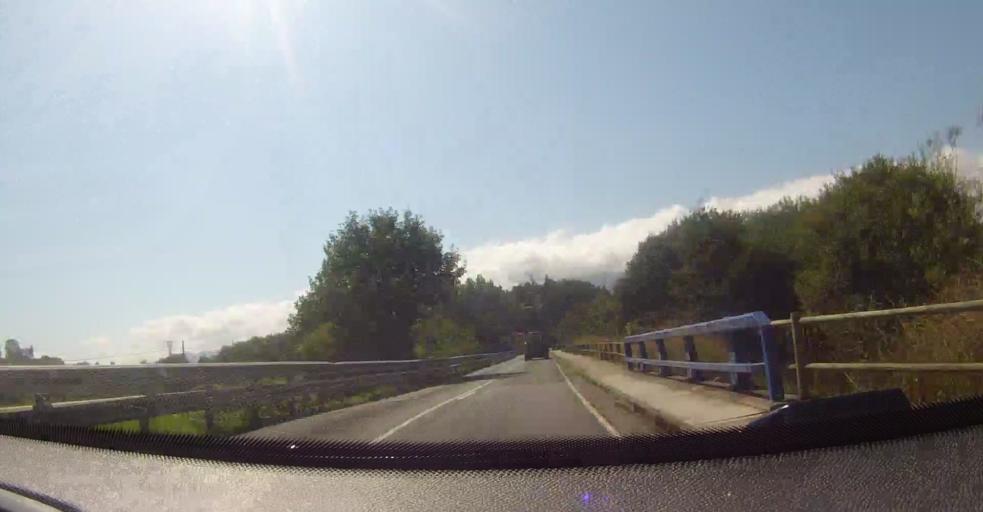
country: ES
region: Asturias
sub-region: Province of Asturias
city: Colunga
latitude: 43.4898
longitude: -5.2778
